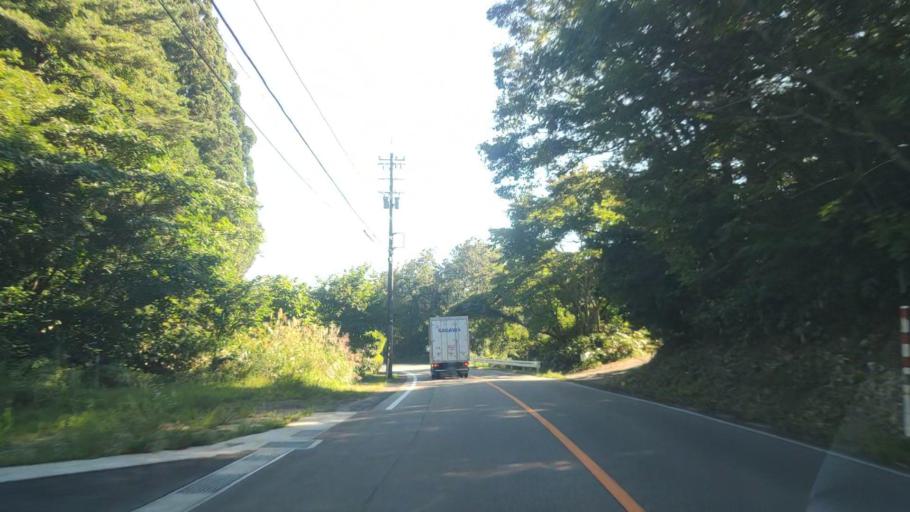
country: JP
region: Ishikawa
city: Nanao
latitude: 37.2113
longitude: 136.9079
